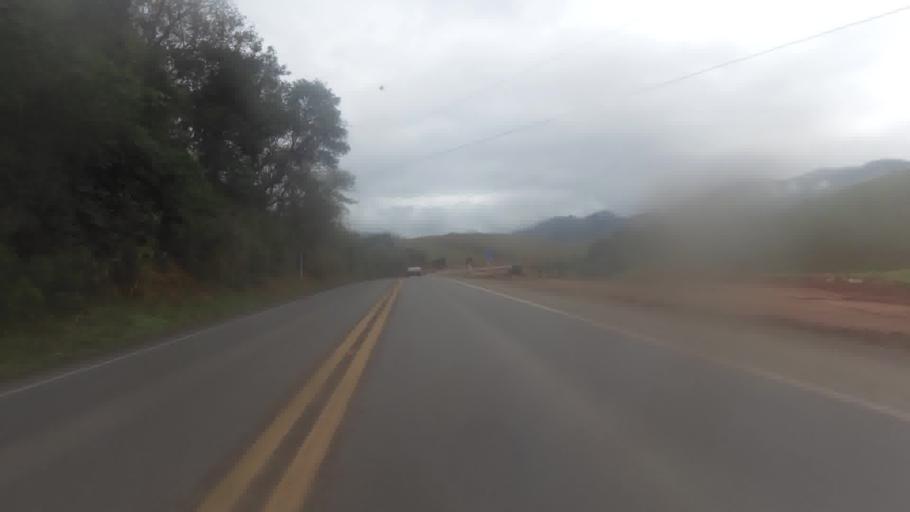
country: BR
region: Espirito Santo
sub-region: Iconha
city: Iconha
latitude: -20.7333
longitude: -40.7494
